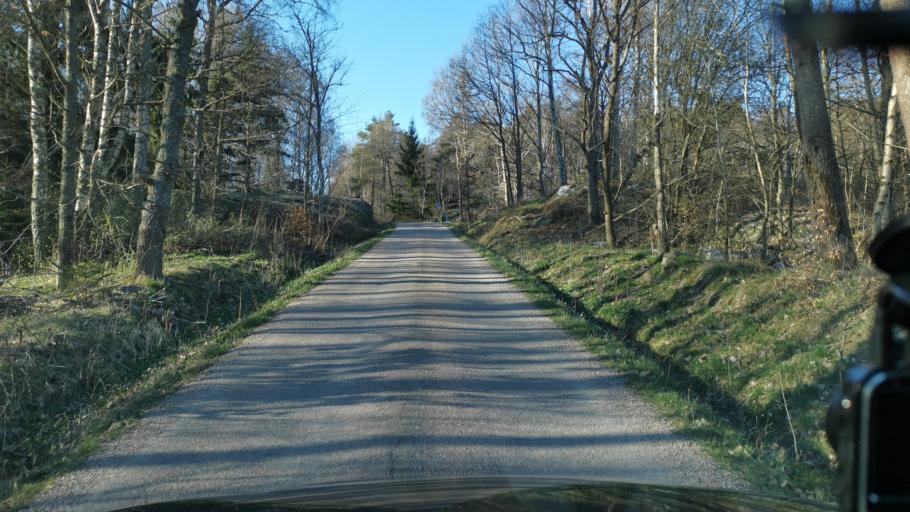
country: SE
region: Vaestra Goetaland
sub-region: Orust
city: Henan
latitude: 58.2784
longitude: 11.6398
